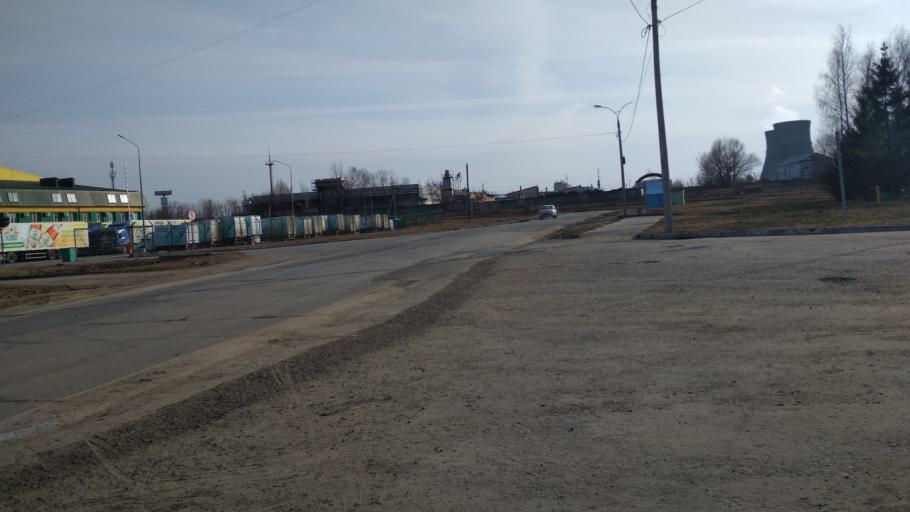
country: RU
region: Chuvashia
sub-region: Cheboksarskiy Rayon
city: Cheboksary
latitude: 56.1344
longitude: 47.3161
